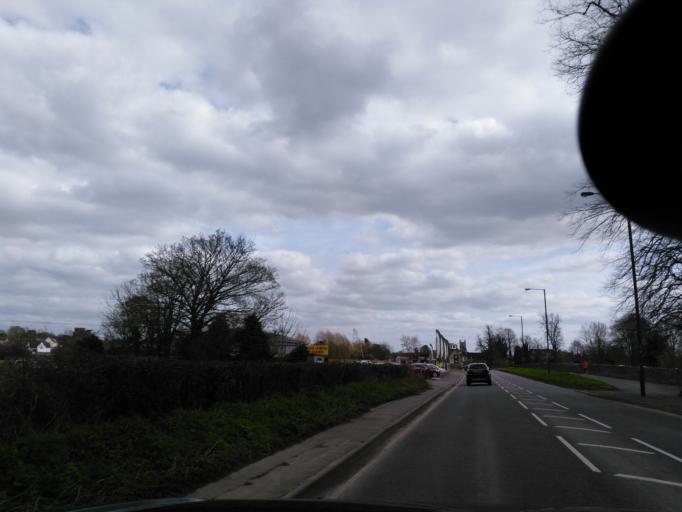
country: GB
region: England
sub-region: Gloucestershire
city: Cirencester
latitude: 51.7253
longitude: -1.9760
